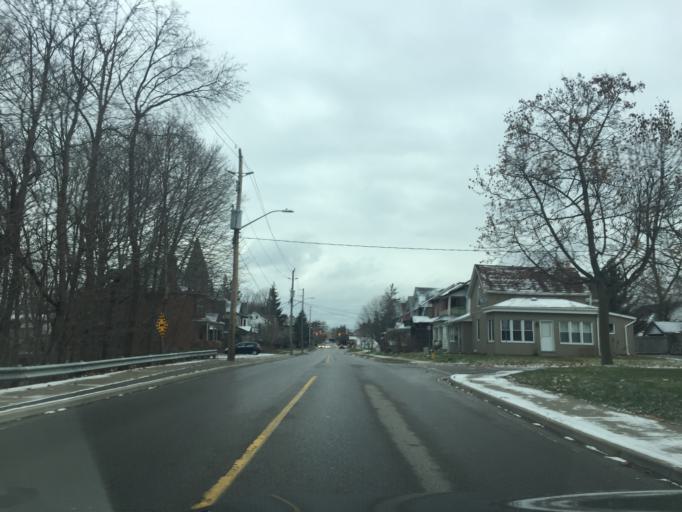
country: CA
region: Ontario
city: St. Thomas
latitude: 42.7733
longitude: -81.1986
